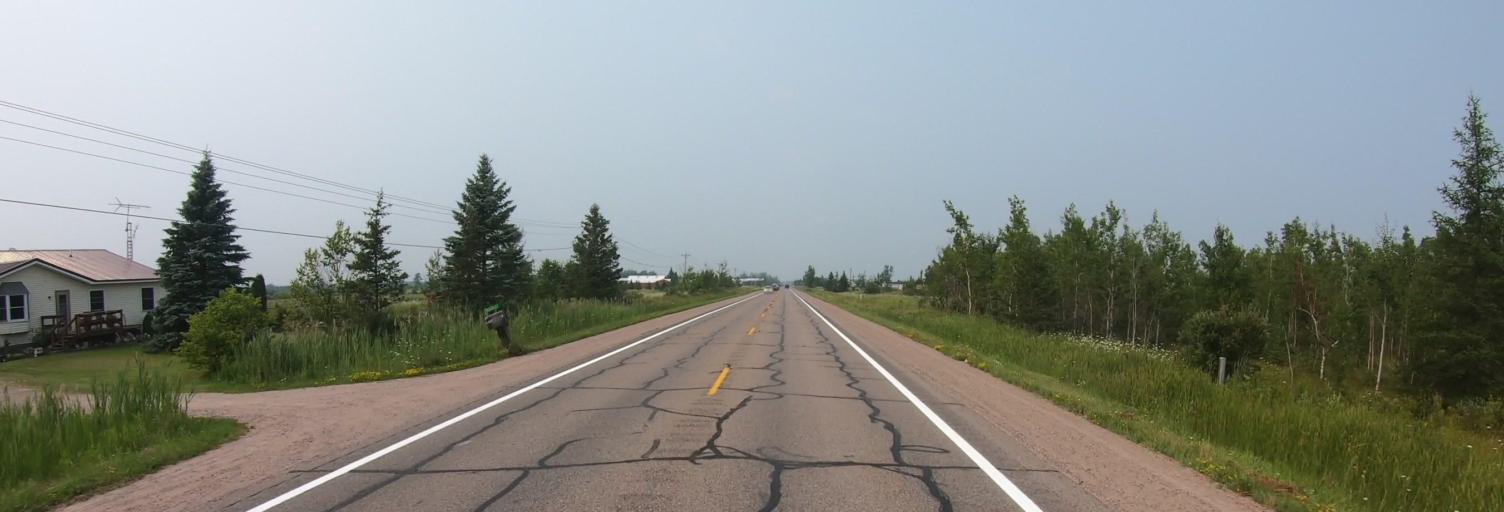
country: US
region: Michigan
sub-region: Chippewa County
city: Sault Ste. Marie
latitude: 46.4286
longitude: -84.3535
